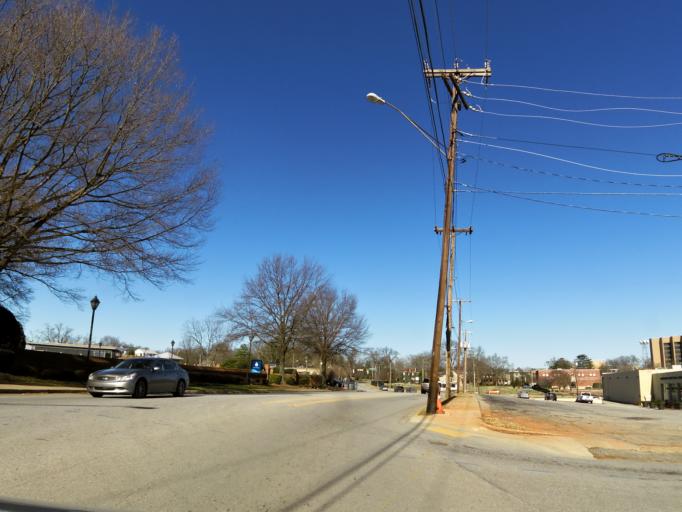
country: US
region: South Carolina
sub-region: Greenville County
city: Greenville
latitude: 34.8514
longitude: -82.4054
